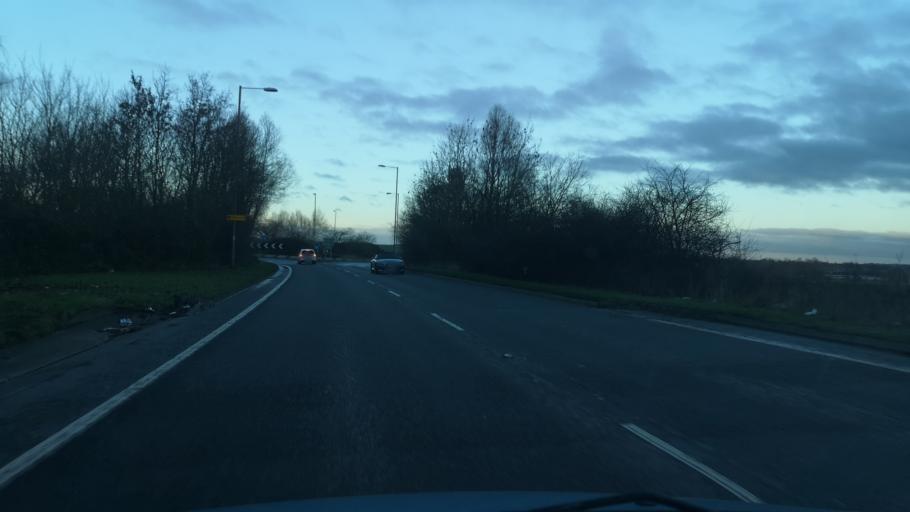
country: GB
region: England
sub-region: City and Borough of Wakefield
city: Hemsworth
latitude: 53.6267
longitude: -1.3371
